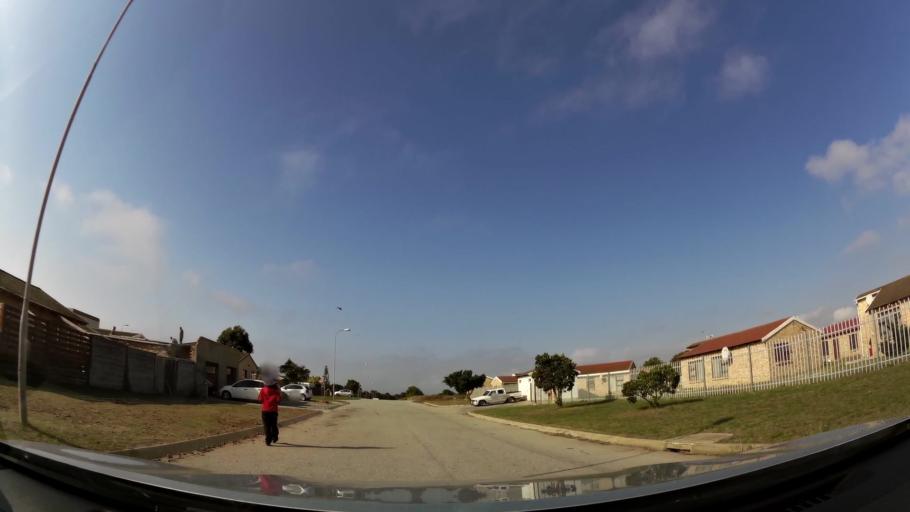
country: ZA
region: Eastern Cape
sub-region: Nelson Mandela Bay Metropolitan Municipality
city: Port Elizabeth
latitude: -33.9183
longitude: 25.5318
